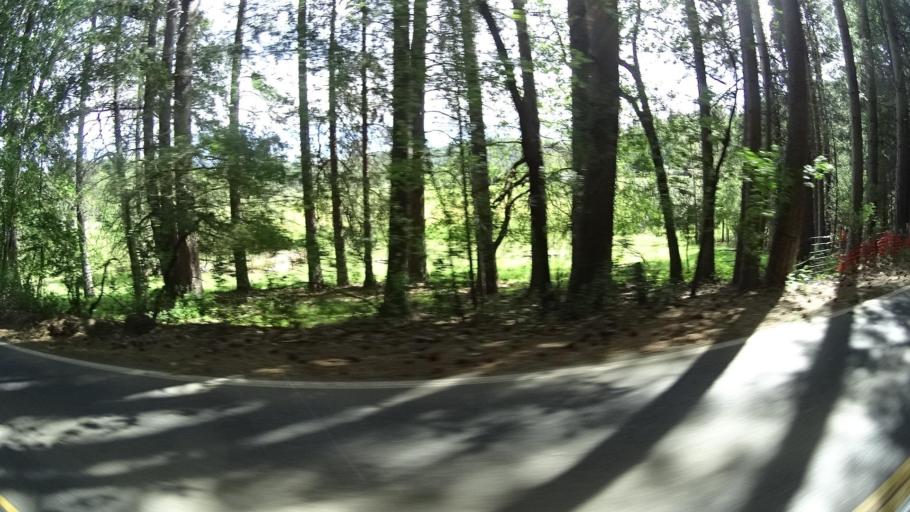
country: US
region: California
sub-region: Lake County
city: Cobb
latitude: 38.8761
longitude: -122.7312
